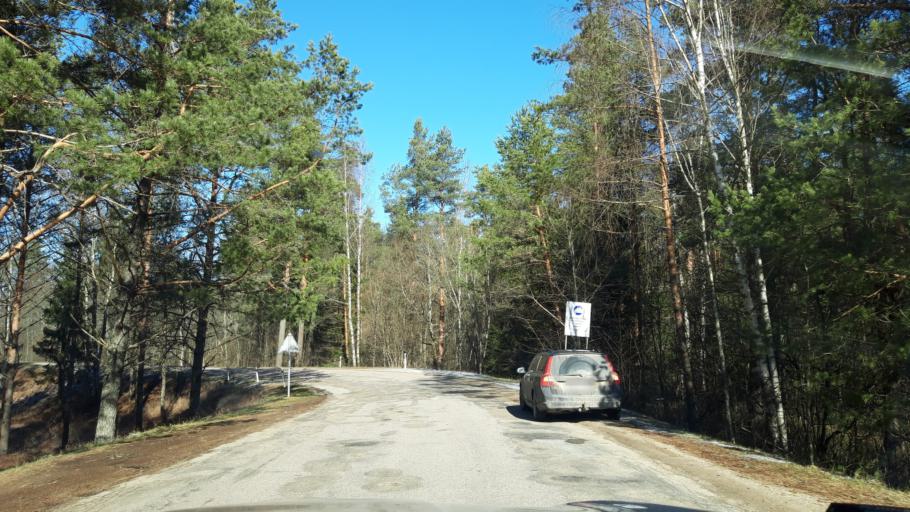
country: LV
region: Strenci
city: Strenci
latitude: 57.6193
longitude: 25.7015
